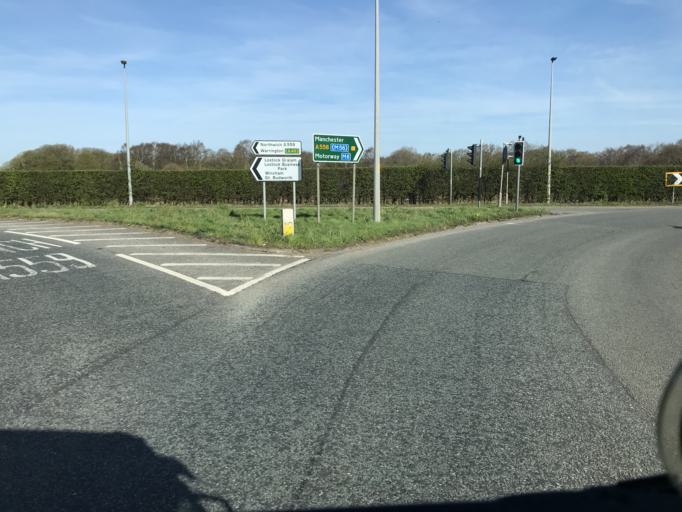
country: GB
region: England
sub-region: Cheshire West and Chester
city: Marston
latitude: 53.2742
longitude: -2.4517
